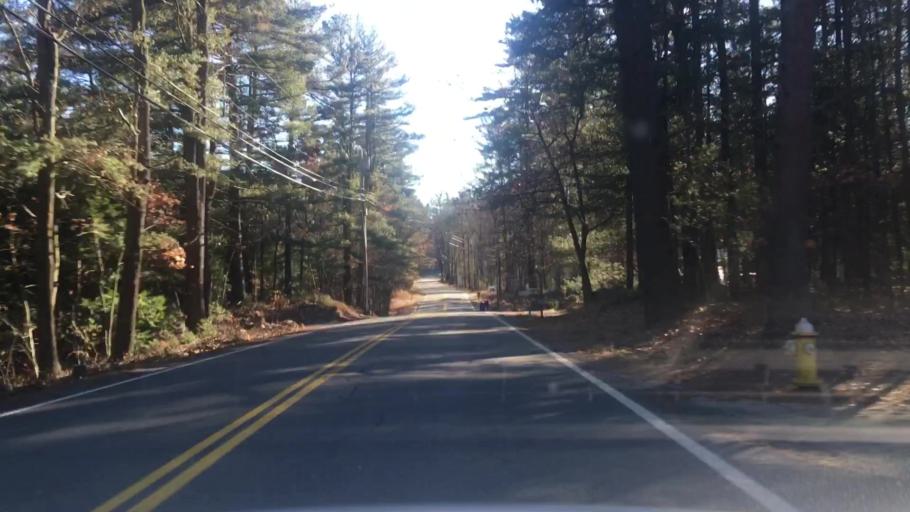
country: US
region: New Hampshire
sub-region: Rockingham County
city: Londonderry
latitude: 42.8932
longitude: -71.4113
